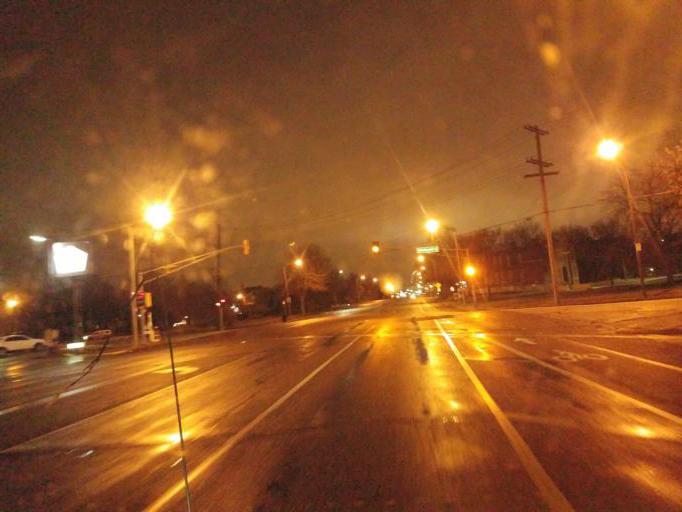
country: US
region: Missouri
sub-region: City of Saint Louis
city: St. Louis
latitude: 38.6553
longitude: -90.2028
